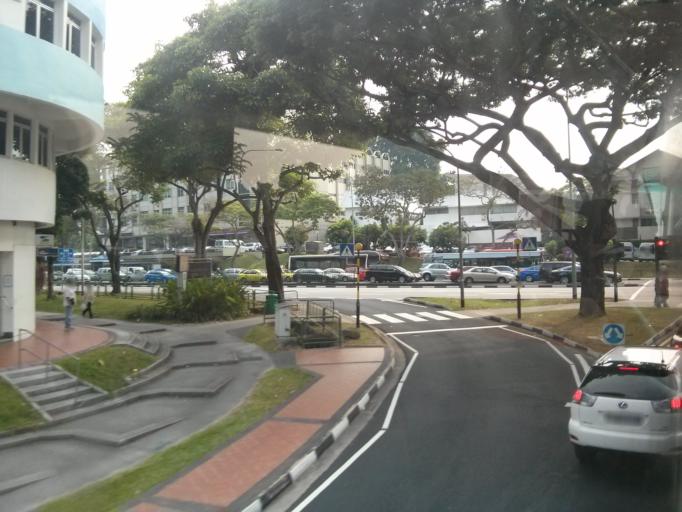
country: SG
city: Singapore
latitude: 1.3264
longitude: 103.8423
